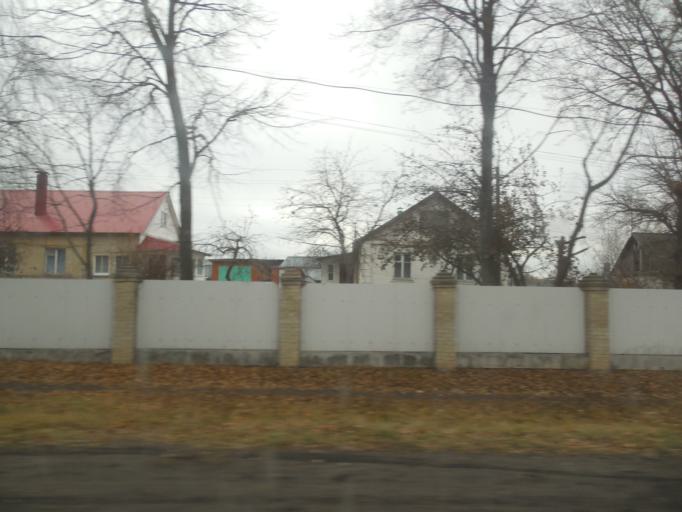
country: RU
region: Tula
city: Dubovka
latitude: 53.9040
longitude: 38.0308
